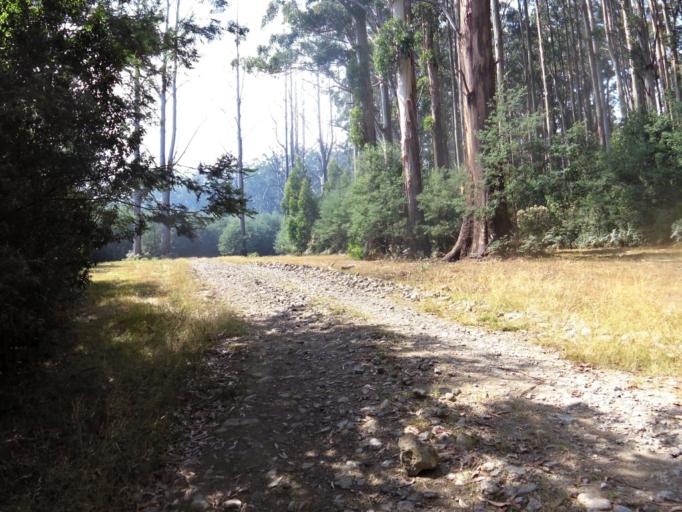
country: AU
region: Victoria
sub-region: Yarra Ranges
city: Healesville
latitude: -37.5660
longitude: 145.5977
